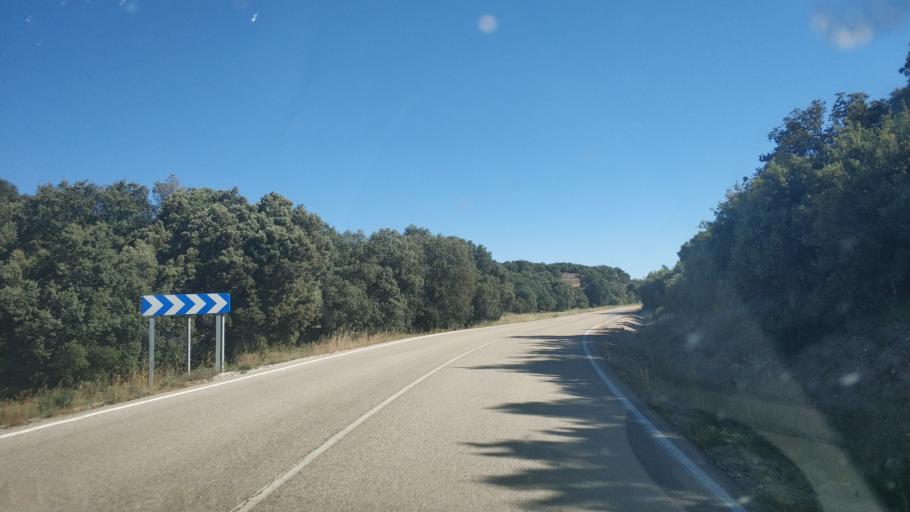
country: ES
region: Castille and Leon
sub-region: Provincia de Soria
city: San Esteban de Gormaz
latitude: 41.5032
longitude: -3.1955
